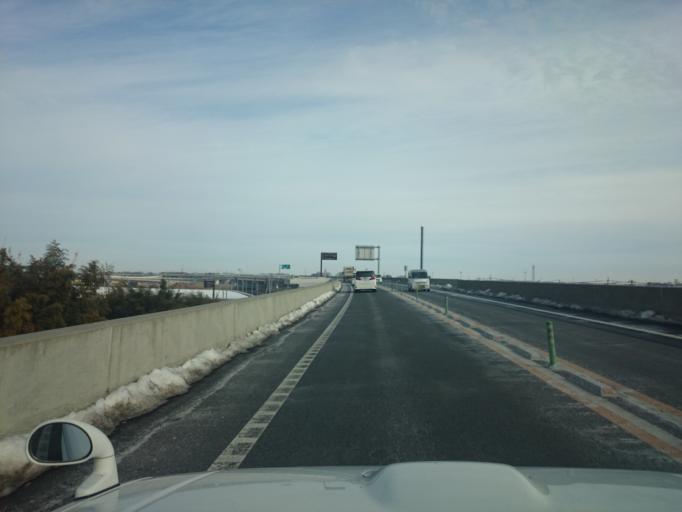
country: JP
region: Saitama
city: Satte
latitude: 36.0890
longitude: 139.7612
